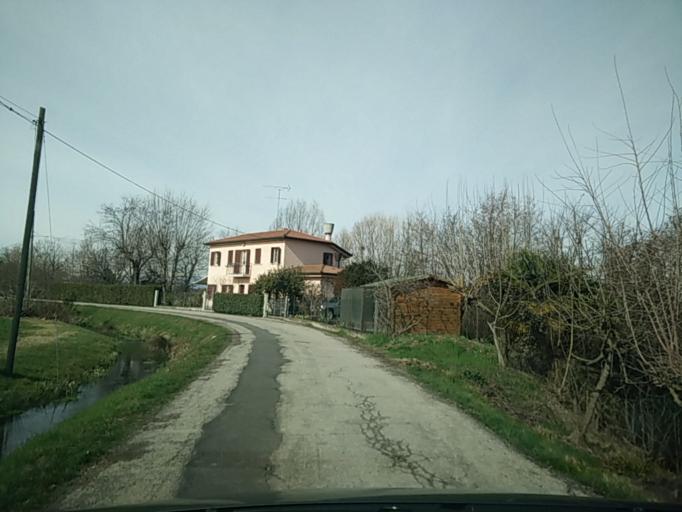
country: IT
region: Veneto
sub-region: Provincia di Treviso
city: Mignagola
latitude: 45.6977
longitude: 12.3191
